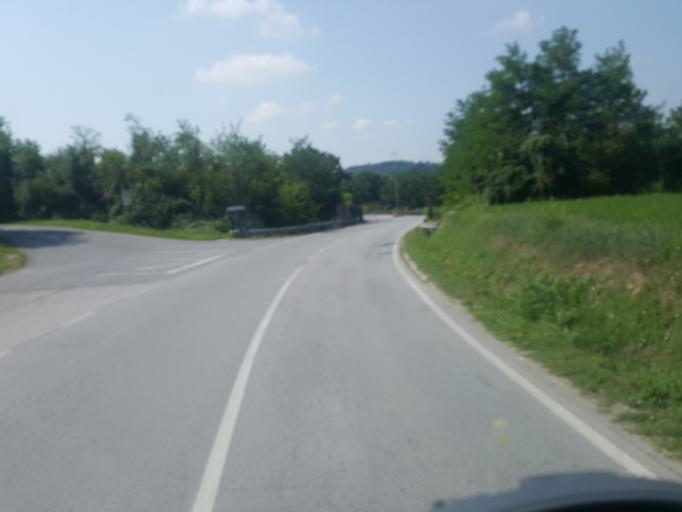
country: IT
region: Piedmont
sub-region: Provincia di Cuneo
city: Narzole
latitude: 44.5985
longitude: 7.8922
